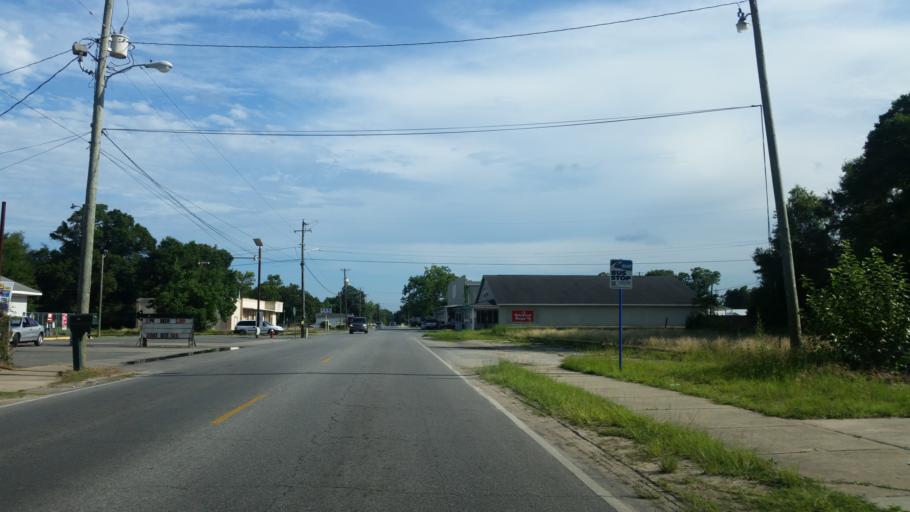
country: US
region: Florida
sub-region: Escambia County
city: Goulding
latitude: 30.4331
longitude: -87.2462
